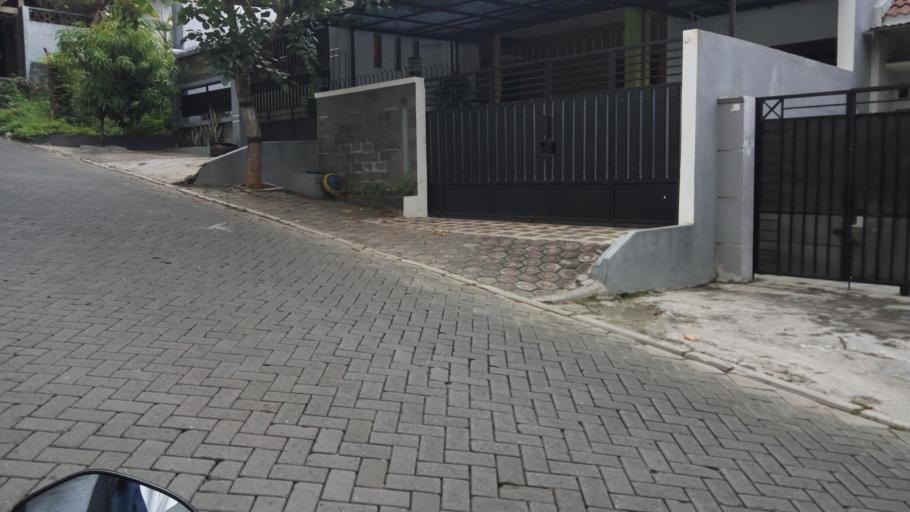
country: ID
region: Central Java
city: Mranggen
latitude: -7.0404
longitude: 110.4759
